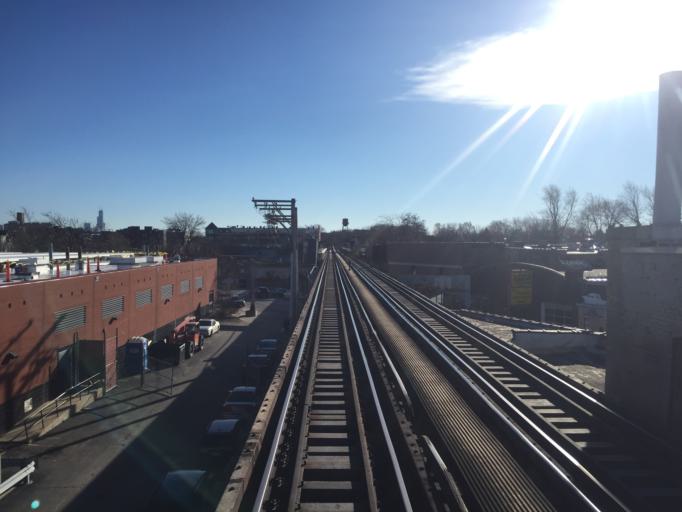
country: US
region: Illinois
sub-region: Cook County
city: Lincolnwood
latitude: 41.9489
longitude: -87.6748
